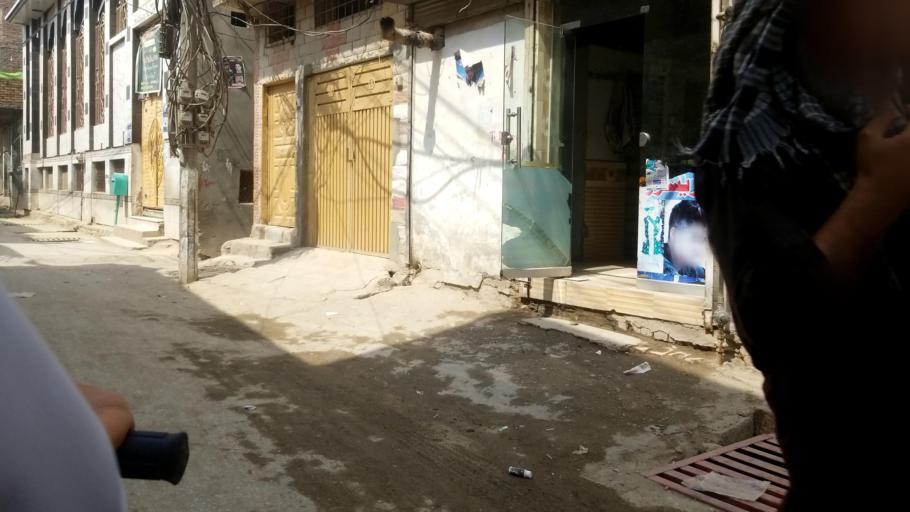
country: PK
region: Khyber Pakhtunkhwa
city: Peshawar
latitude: 33.9917
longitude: 71.5449
